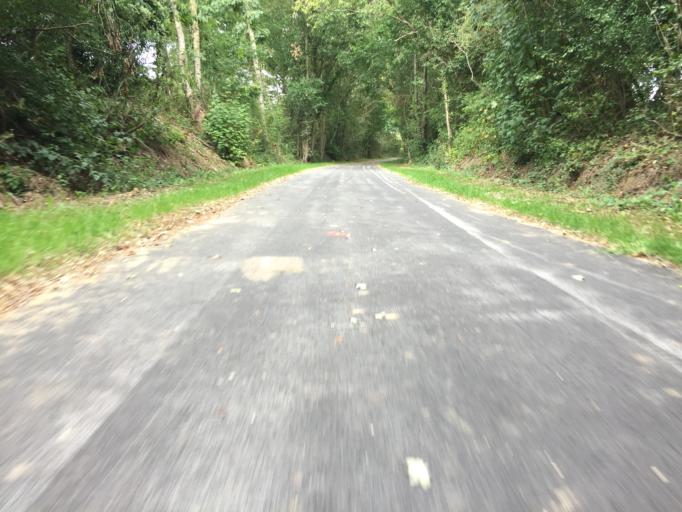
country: FR
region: Picardie
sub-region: Departement de l'Oise
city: Auneuil
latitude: 49.3800
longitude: 1.9925
